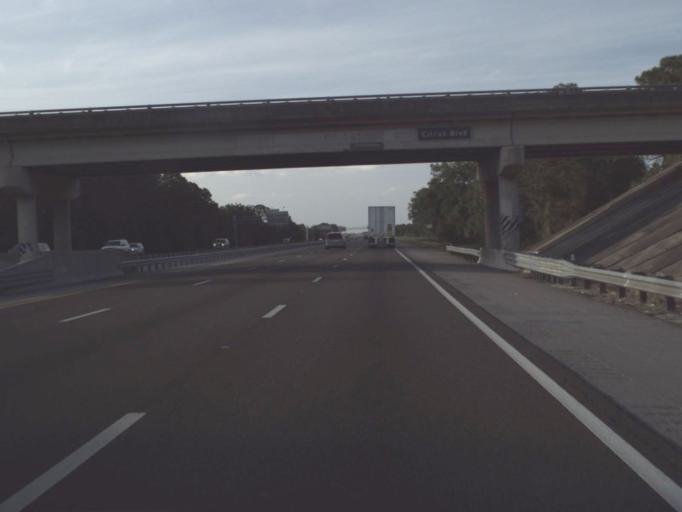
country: US
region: Florida
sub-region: Brevard County
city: Sharpes
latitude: 28.4244
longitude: -80.8202
